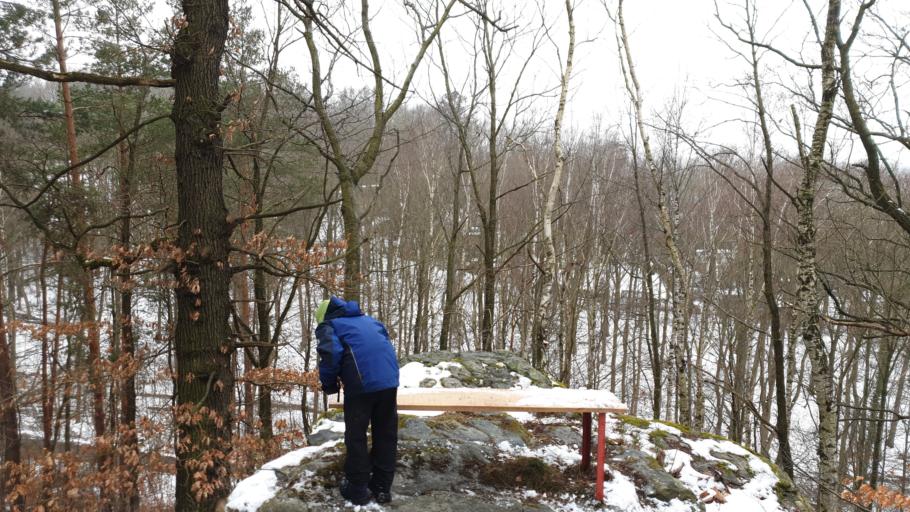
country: DE
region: Saxony
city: Gornau
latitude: 50.7724
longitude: 12.9801
